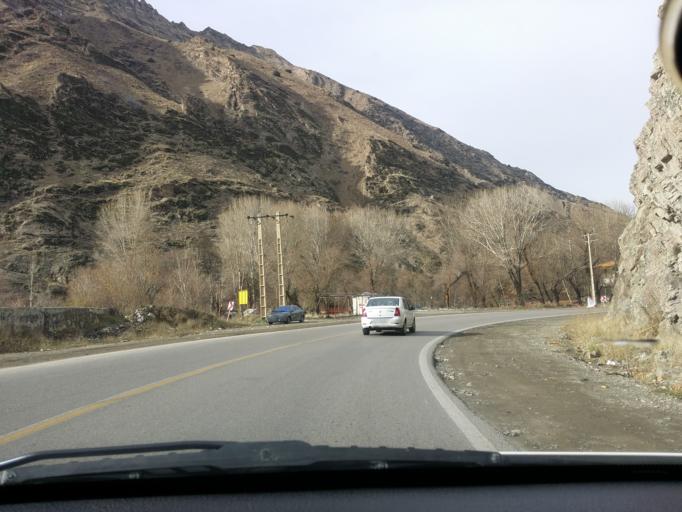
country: IR
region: Tehran
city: Tajrish
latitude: 36.0281
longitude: 51.2409
